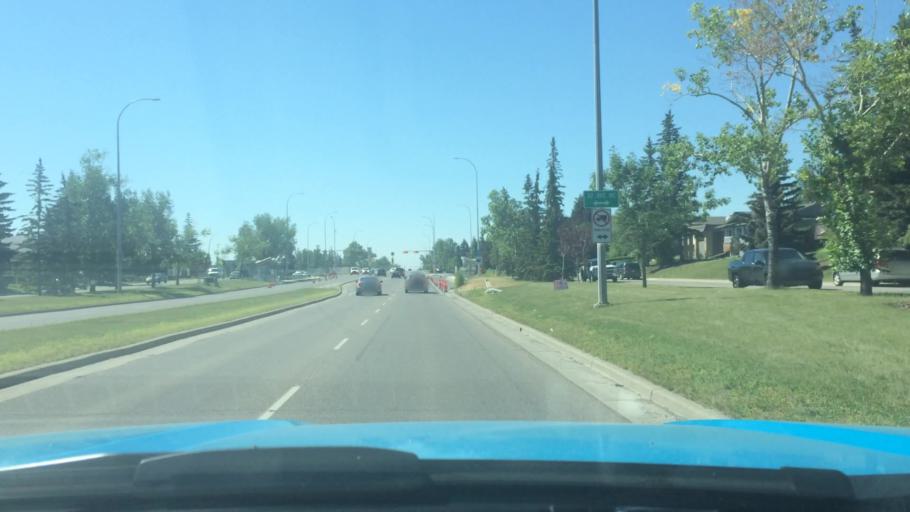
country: CA
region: Alberta
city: Calgary
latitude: 51.0835
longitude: -113.9584
